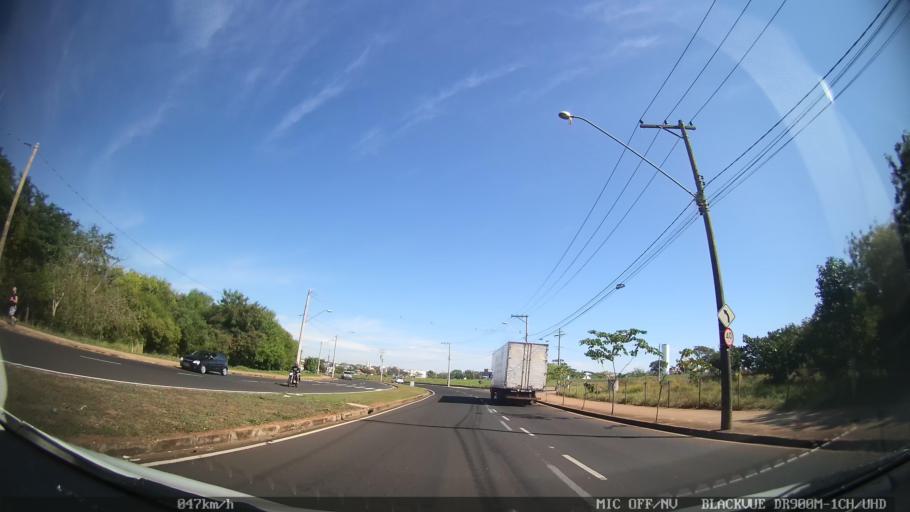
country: BR
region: Sao Paulo
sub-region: Sao Jose Do Rio Preto
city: Sao Jose do Rio Preto
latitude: -20.8048
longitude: -49.4243
